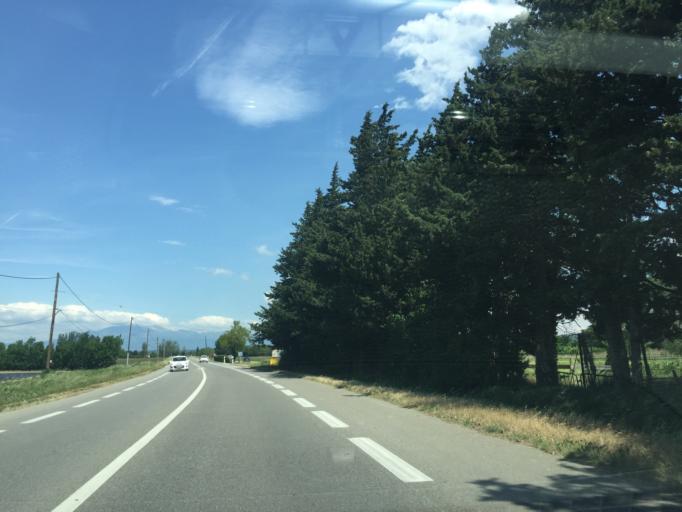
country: FR
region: Provence-Alpes-Cote d'Azur
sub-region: Departement du Vaucluse
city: Velleron
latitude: 43.9851
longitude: 5.0255
